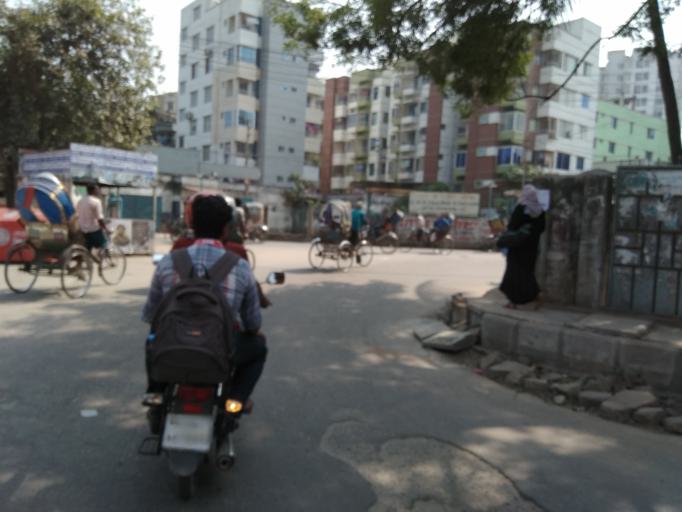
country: BD
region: Dhaka
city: Paltan
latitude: 23.7221
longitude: 90.4176
